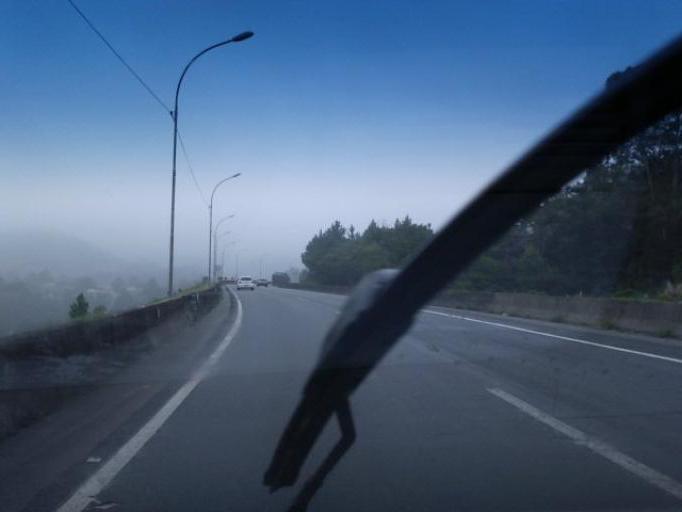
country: BR
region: Parana
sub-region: Campina Grande Do Sul
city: Campina Grande do Sul
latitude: -25.1121
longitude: -48.8139
